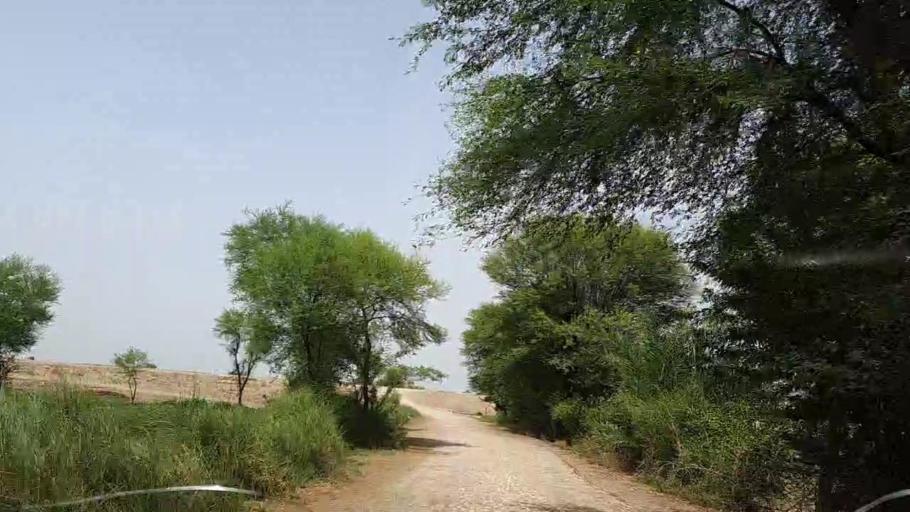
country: PK
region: Sindh
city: Tharu Shah
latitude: 26.9964
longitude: 68.0808
